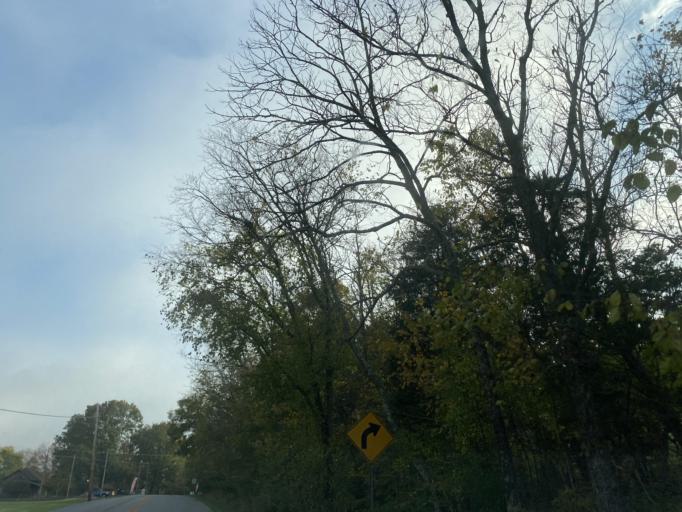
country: US
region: Kentucky
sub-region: Pendleton County
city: Falmouth
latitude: 38.7209
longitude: -84.2936
